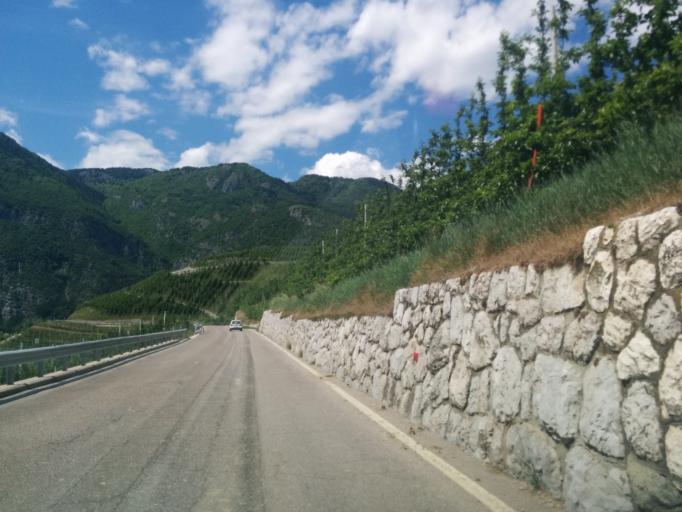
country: IT
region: Trentino-Alto Adige
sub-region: Provincia di Trento
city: Terres
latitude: 46.3181
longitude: 11.0235
